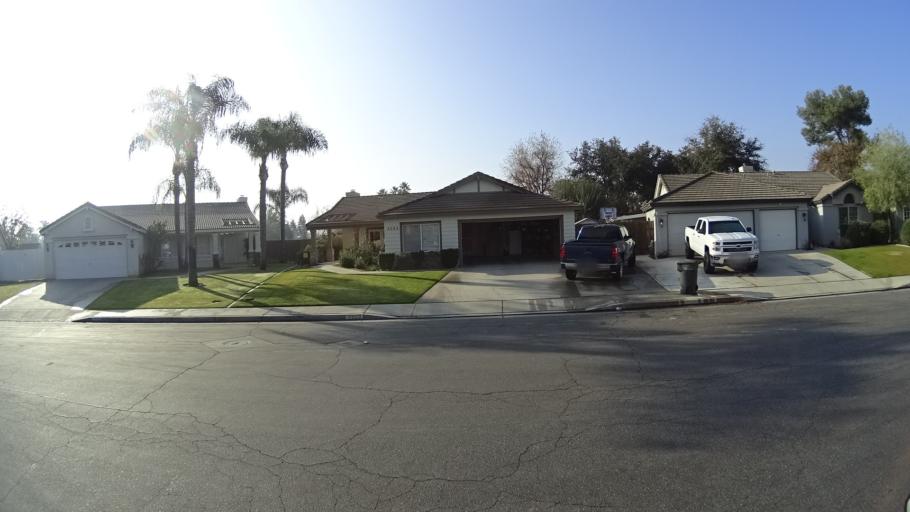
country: US
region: California
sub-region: Kern County
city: Greenacres
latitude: 35.3919
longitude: -119.1017
